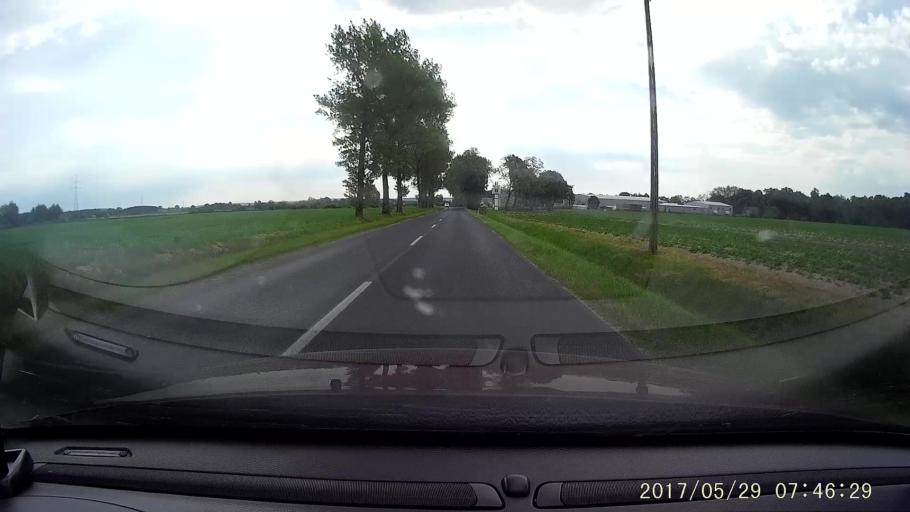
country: PL
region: Lower Silesian Voivodeship
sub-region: Powiat boleslawiecki
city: Boleslawiec
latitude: 51.2363
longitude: 15.6485
